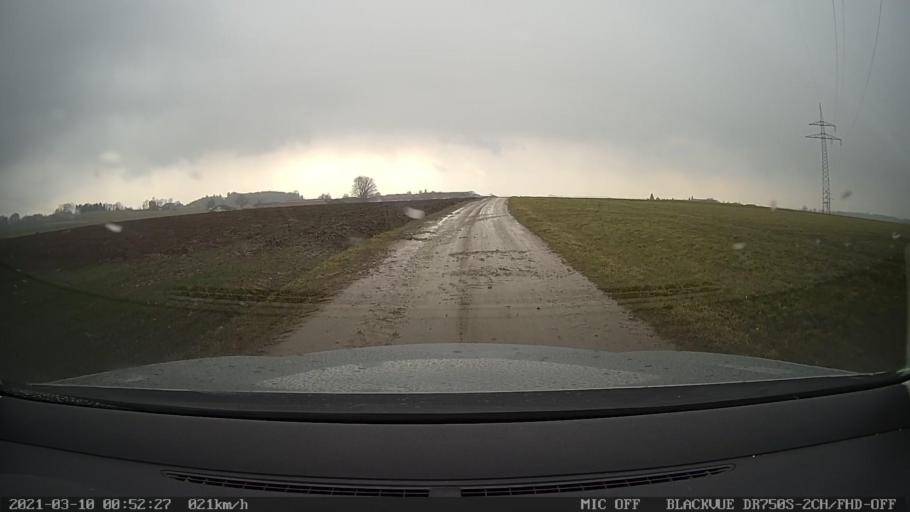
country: DE
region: Bavaria
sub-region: Upper Bavaria
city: Griesstatt
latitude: 47.9925
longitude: 12.1928
